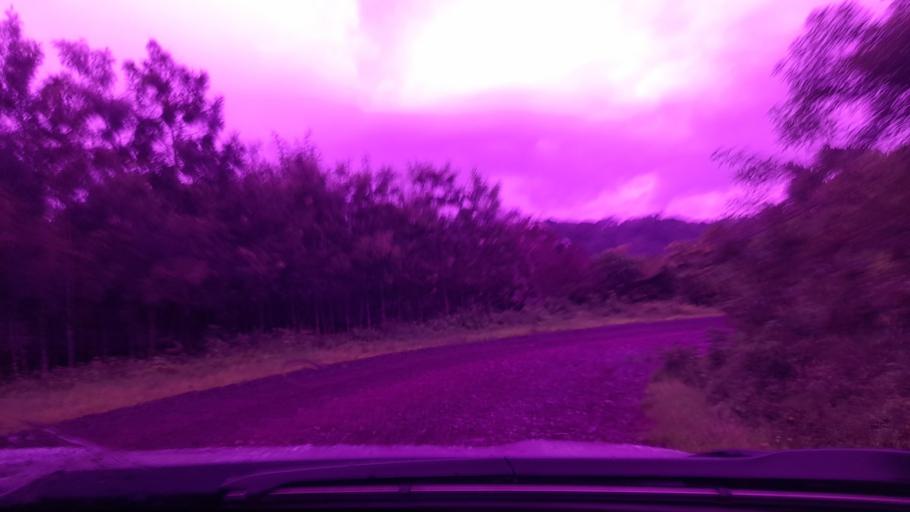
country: ET
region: Oromiya
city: Metu
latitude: 8.4513
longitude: 35.6332
